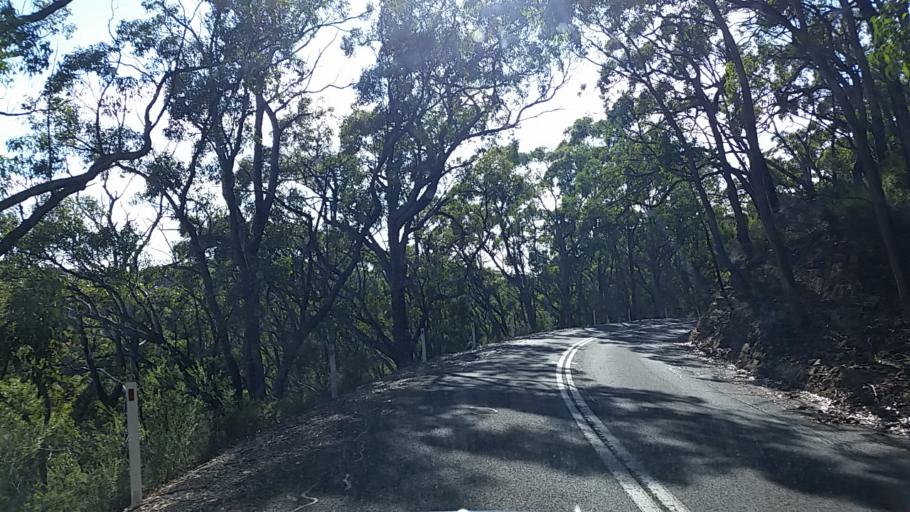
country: AU
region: South Australia
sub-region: Adelaide Hills
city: Crafers
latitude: -34.9662
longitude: 138.7108
